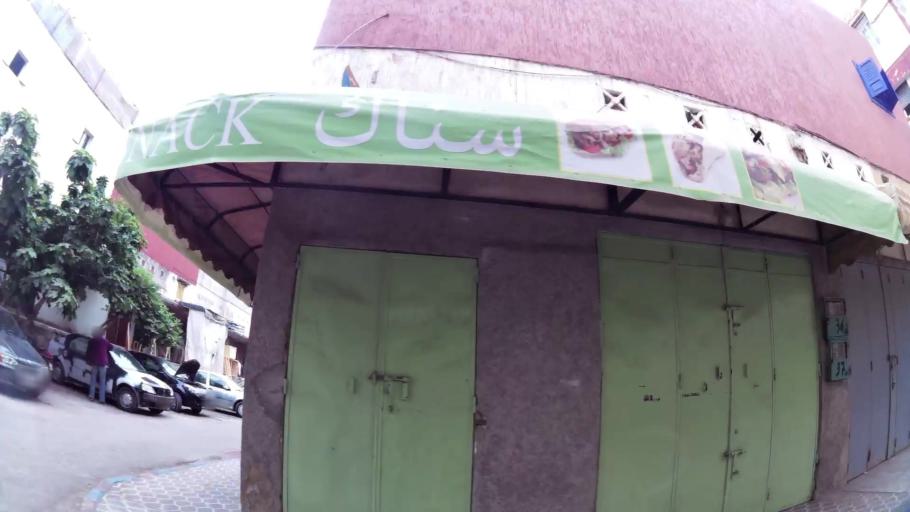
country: MA
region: Rabat-Sale-Zemmour-Zaer
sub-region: Rabat
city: Rabat
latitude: 33.9927
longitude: -6.8698
